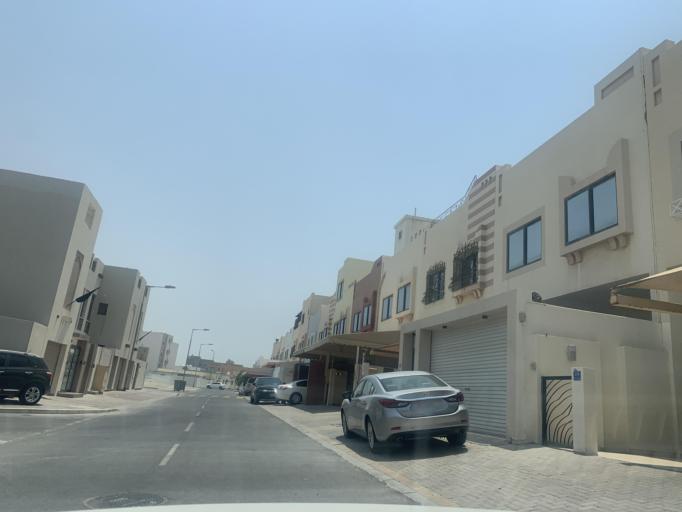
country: BH
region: Central Governorate
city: Madinat Hamad
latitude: 26.1458
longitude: 50.4612
